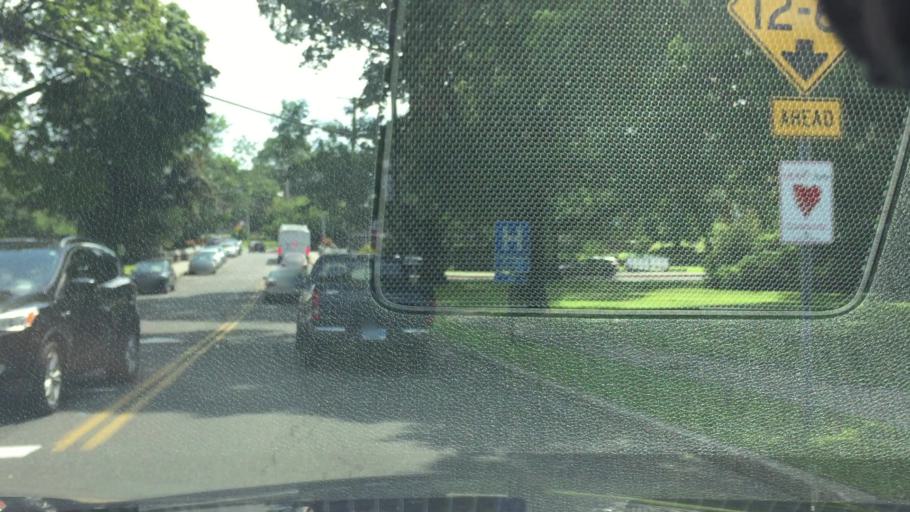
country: US
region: Connecticut
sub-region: New Haven County
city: Milford
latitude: 41.2262
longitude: -73.0567
